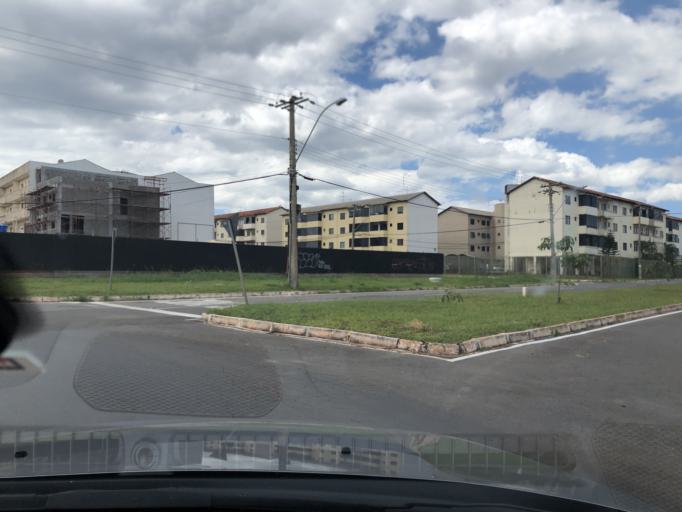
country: BR
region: Federal District
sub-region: Brasilia
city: Brasilia
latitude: -15.9950
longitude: -47.9970
